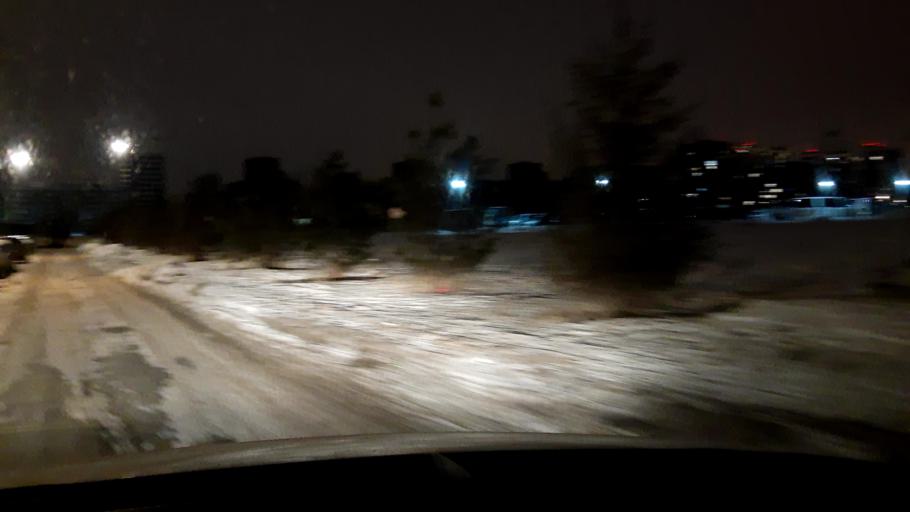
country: RU
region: Moskovskaya
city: Kommunarka
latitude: 55.5504
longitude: 37.5114
